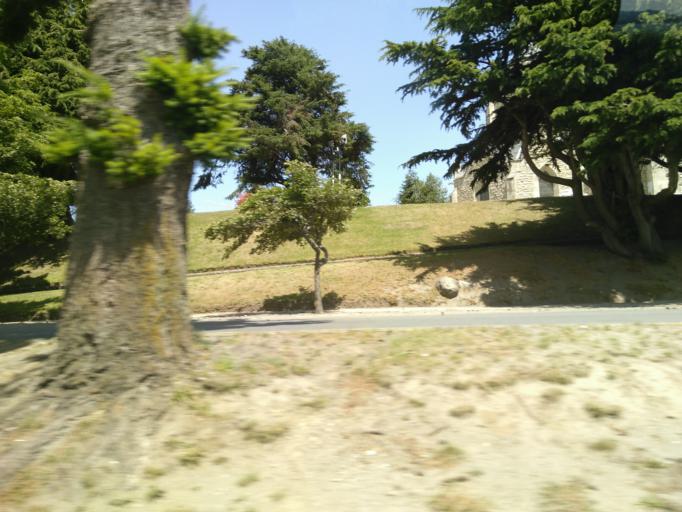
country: AR
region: Rio Negro
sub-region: Departamento de Bariloche
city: San Carlos de Bariloche
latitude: -41.1324
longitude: -71.3021
